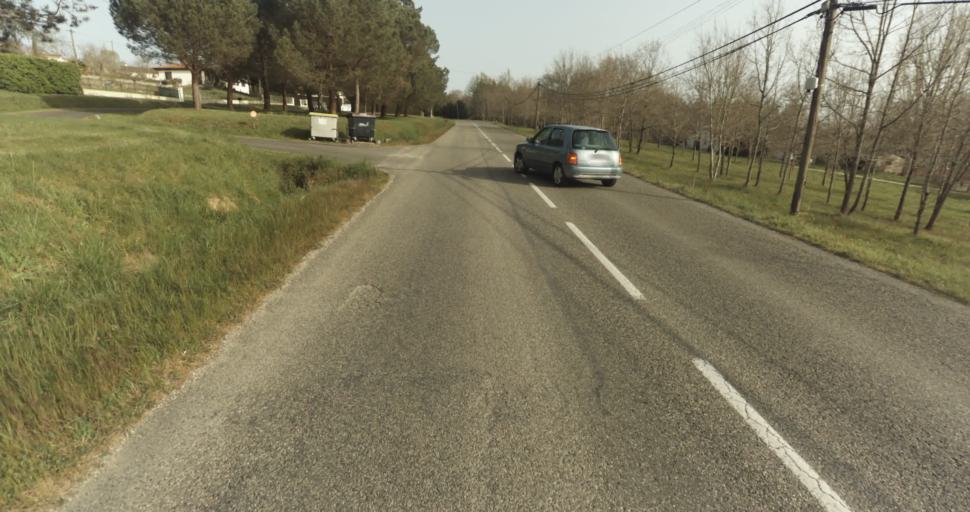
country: FR
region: Midi-Pyrenees
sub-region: Departement du Tarn-et-Garonne
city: Moissac
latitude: 44.1431
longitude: 1.1025
